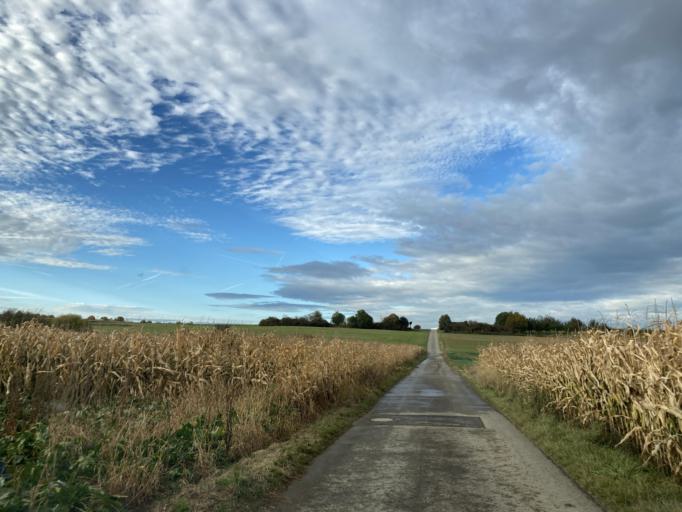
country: DE
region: Baden-Wuerttemberg
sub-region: Regierungsbezirk Stuttgart
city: Bondorf
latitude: 48.4906
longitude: 8.8248
